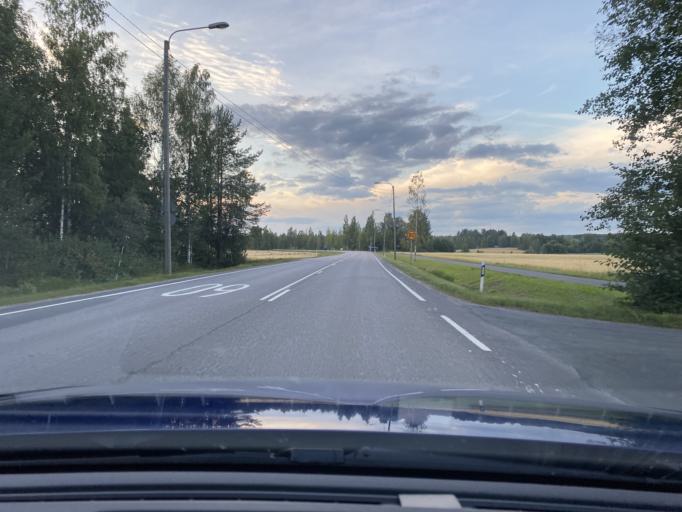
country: FI
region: Satakunta
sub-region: Pohjois-Satakunta
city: Kankaanpaeae
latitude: 61.7571
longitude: 22.5047
